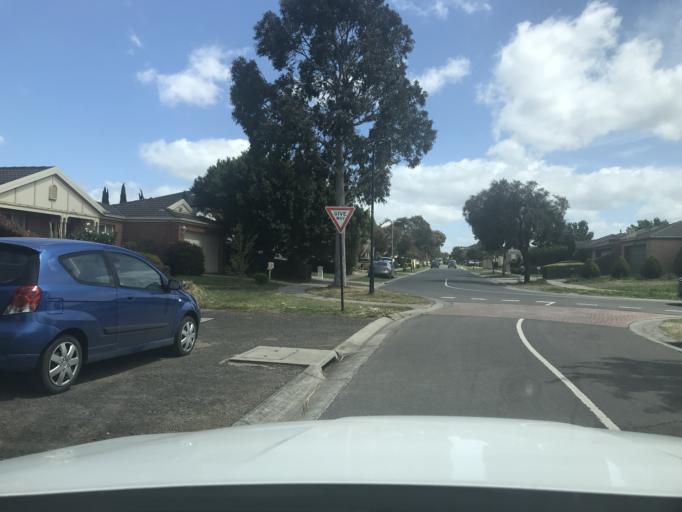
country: AU
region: Victoria
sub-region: Hume
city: Roxburgh Park
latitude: -37.6173
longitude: 144.9347
